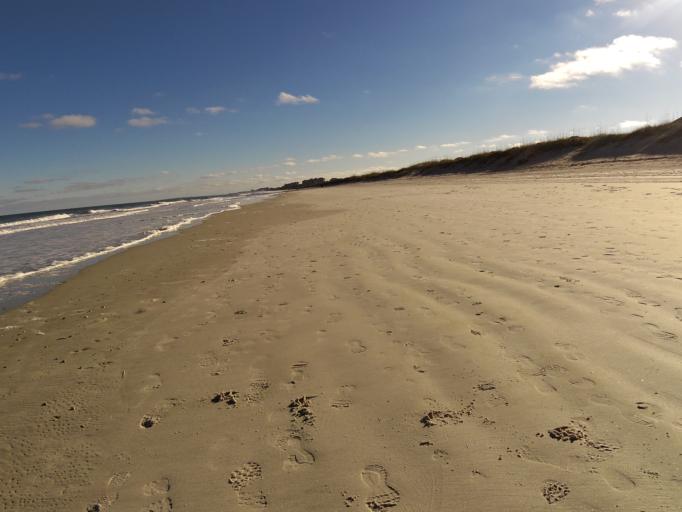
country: US
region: Florida
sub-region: Nassau County
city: Fernandina Beach
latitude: 30.5811
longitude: -81.4430
